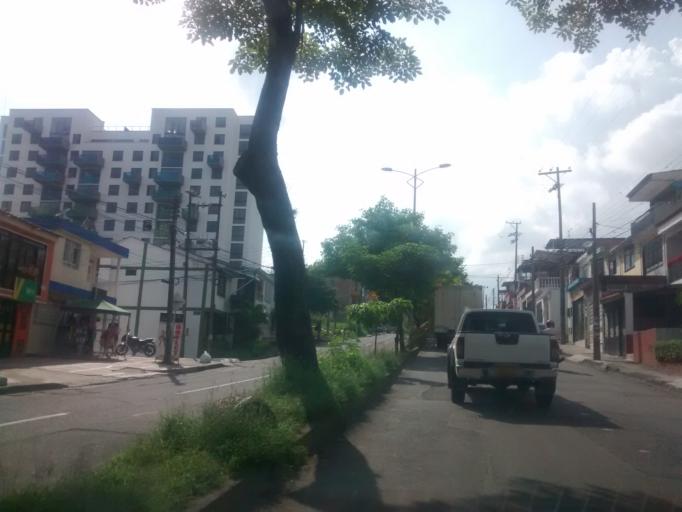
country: CO
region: Tolima
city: Ibague
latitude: 4.4419
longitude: -75.2006
